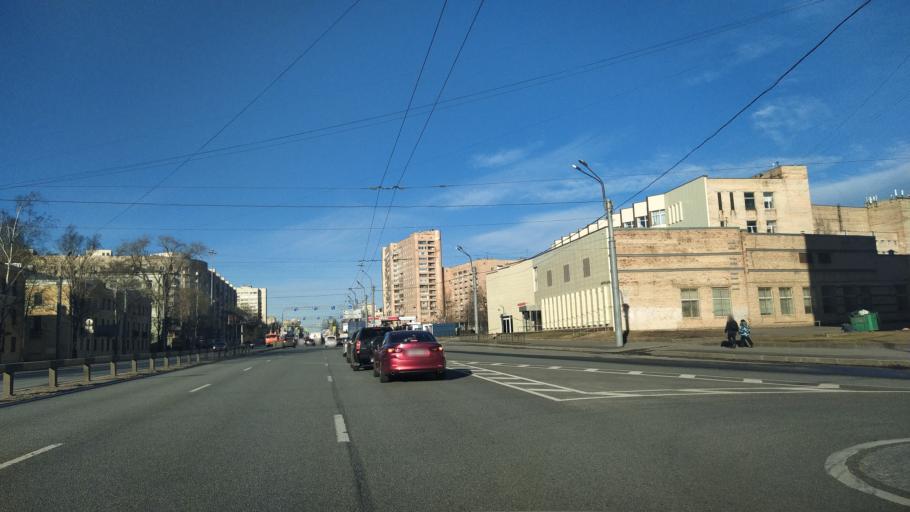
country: RU
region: Leningrad
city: Kalininskiy
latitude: 59.9941
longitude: 30.3787
